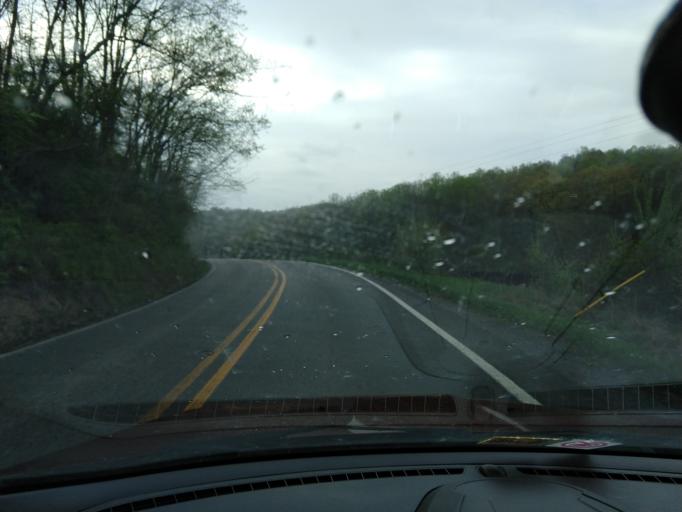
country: US
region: West Virginia
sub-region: Harrison County
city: Despard
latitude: 39.3337
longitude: -80.2866
